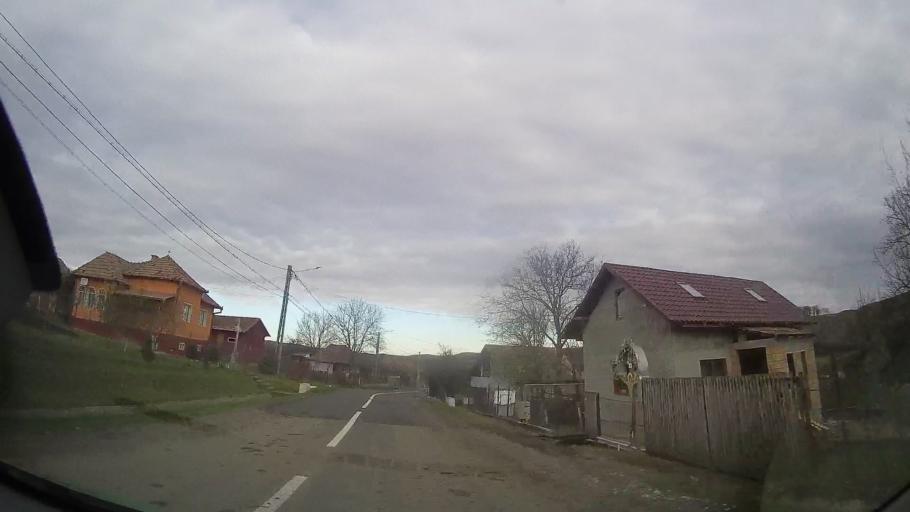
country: RO
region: Bistrita-Nasaud
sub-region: Comuna Micestii de Campie
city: Micestii de Campie
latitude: 46.8560
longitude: 24.3107
